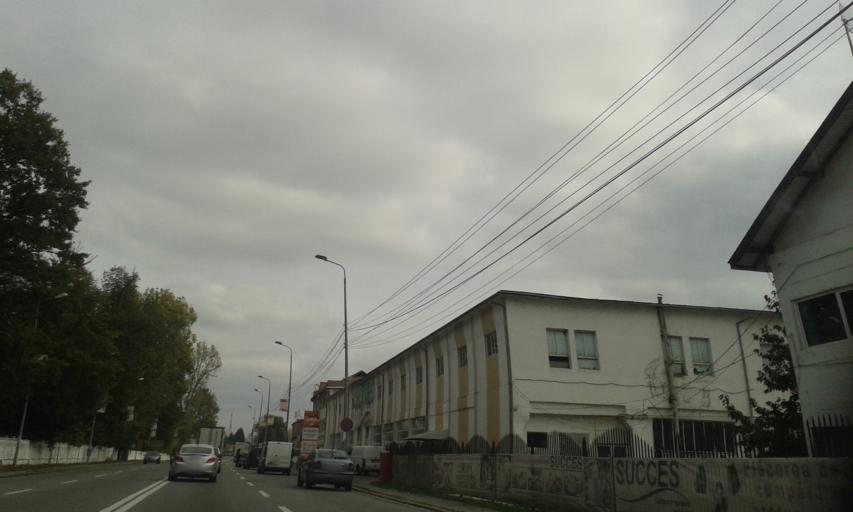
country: RO
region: Gorj
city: Targu Jiu
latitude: 45.0374
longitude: 23.2933
